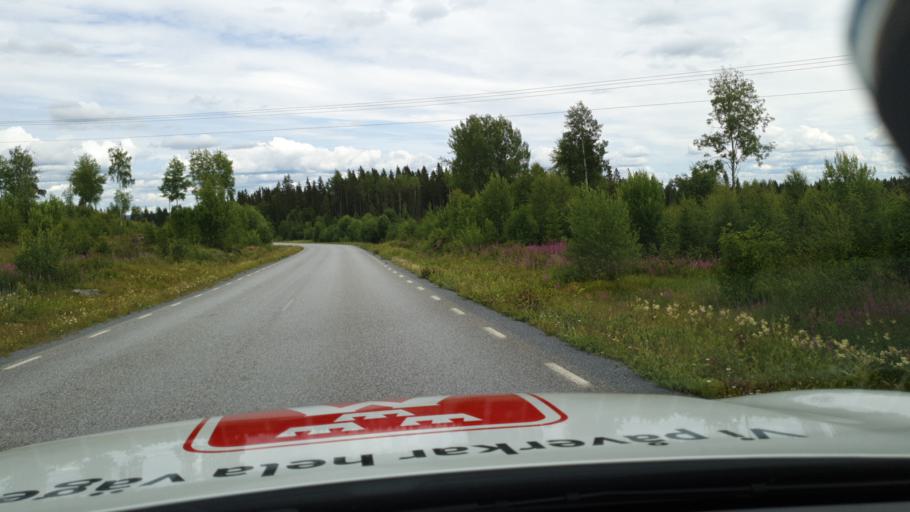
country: SE
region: Jaemtland
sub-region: OEstersunds Kommun
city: Lit
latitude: 63.3273
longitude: 14.8406
